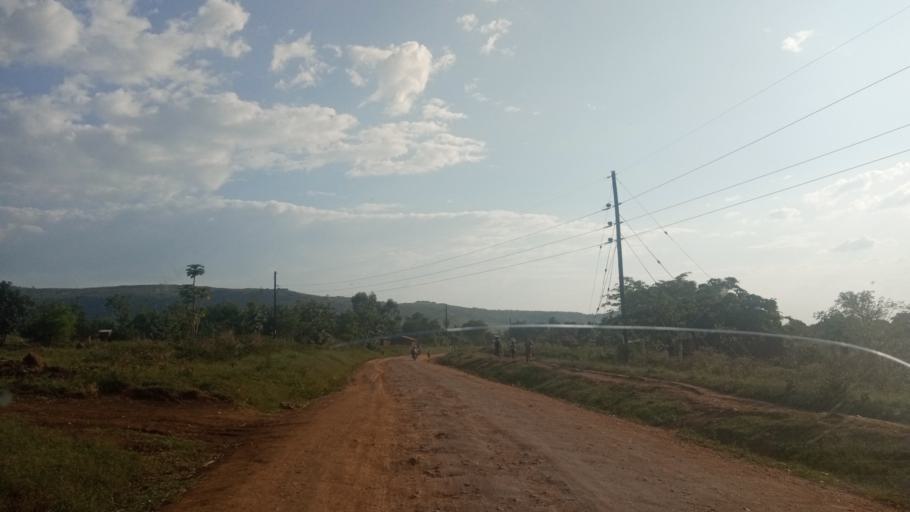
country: UG
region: Eastern Region
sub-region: Kapchorwa District
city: Kapchorwa
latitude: 1.4093
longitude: 34.3475
